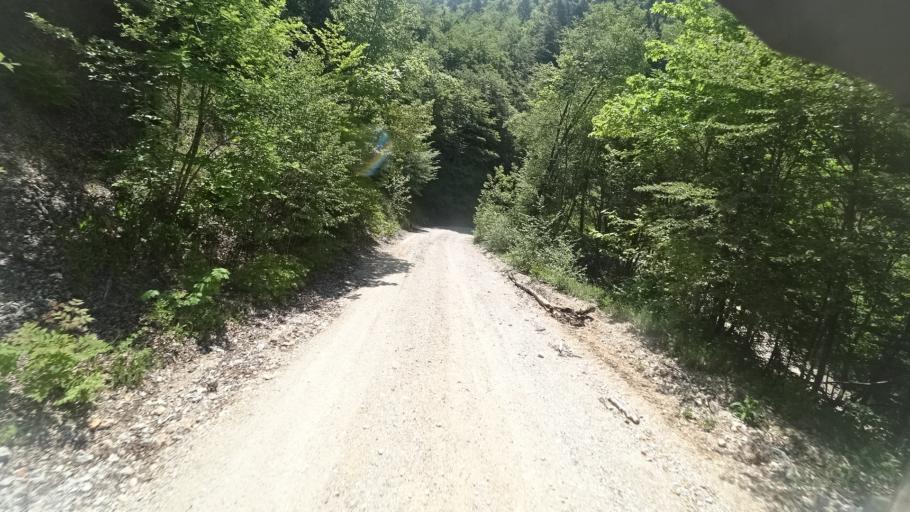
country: BA
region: Federation of Bosnia and Herzegovina
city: Orasac
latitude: 44.5726
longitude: 15.8582
